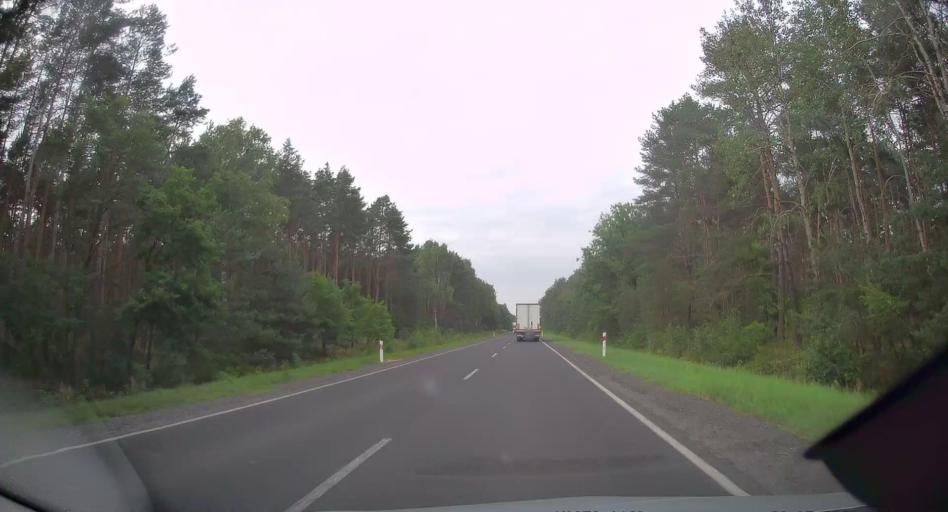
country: PL
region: Lodz Voivodeship
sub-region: Powiat radomszczanski
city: Plawno
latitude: 51.0034
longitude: 19.4186
